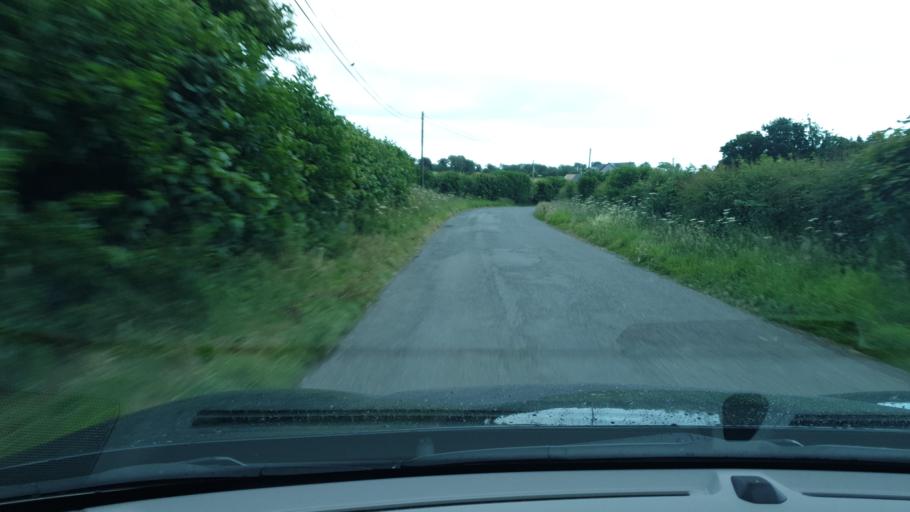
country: IE
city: Kentstown
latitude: 53.5982
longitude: -6.5860
